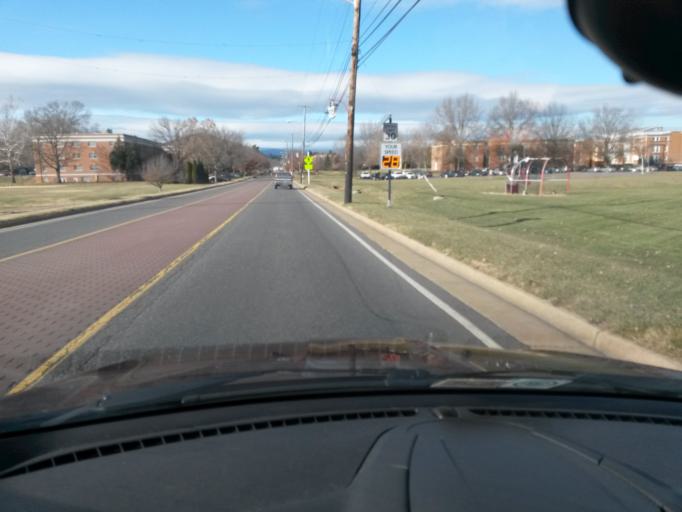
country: US
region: Virginia
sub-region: Rockingham County
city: Bridgewater
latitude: 38.3778
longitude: -78.9658
